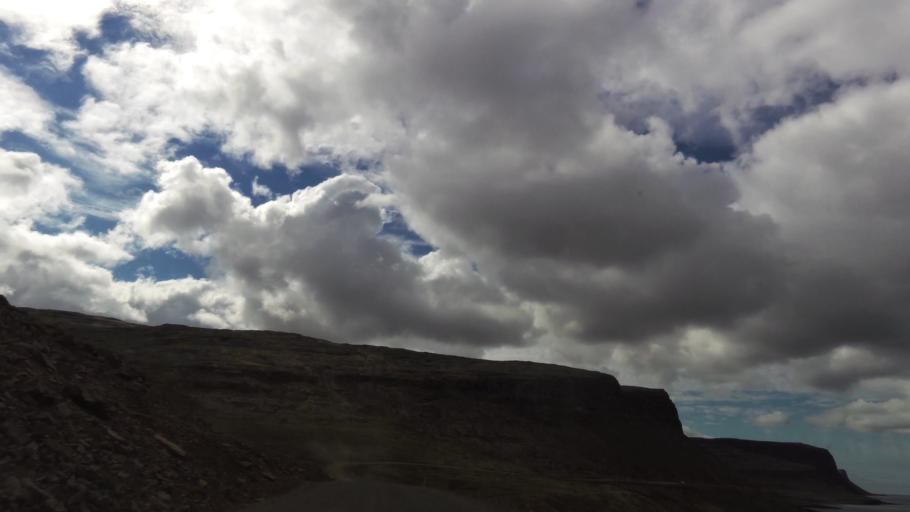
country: IS
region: West
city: Olafsvik
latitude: 65.5615
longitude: -24.0260
